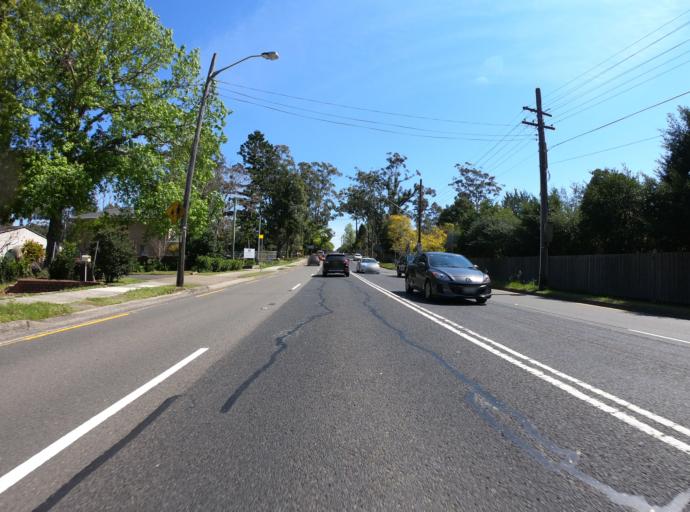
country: AU
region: New South Wales
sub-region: The Hills Shire
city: West Pennant
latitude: -33.7414
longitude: 151.0419
